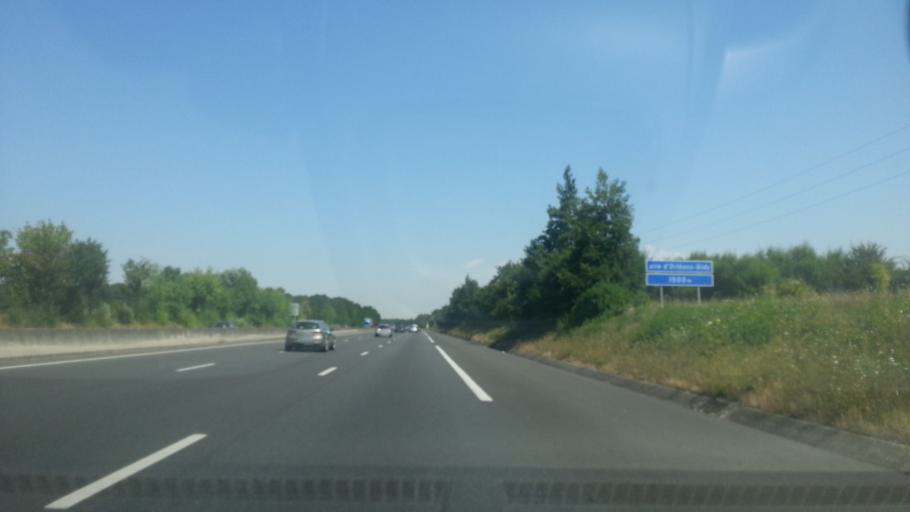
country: FR
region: Centre
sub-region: Departement du Loiret
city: Saran
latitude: 47.9600
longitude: 1.8532
